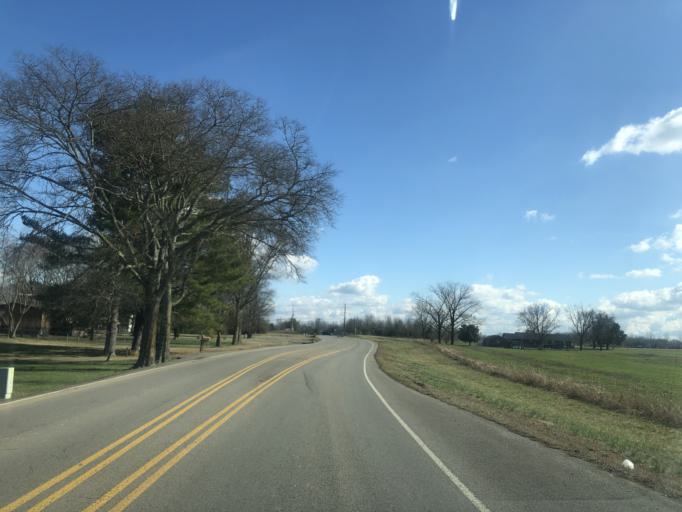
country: US
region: Tennessee
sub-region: Rutherford County
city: Smyrna
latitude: 35.8757
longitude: -86.5013
